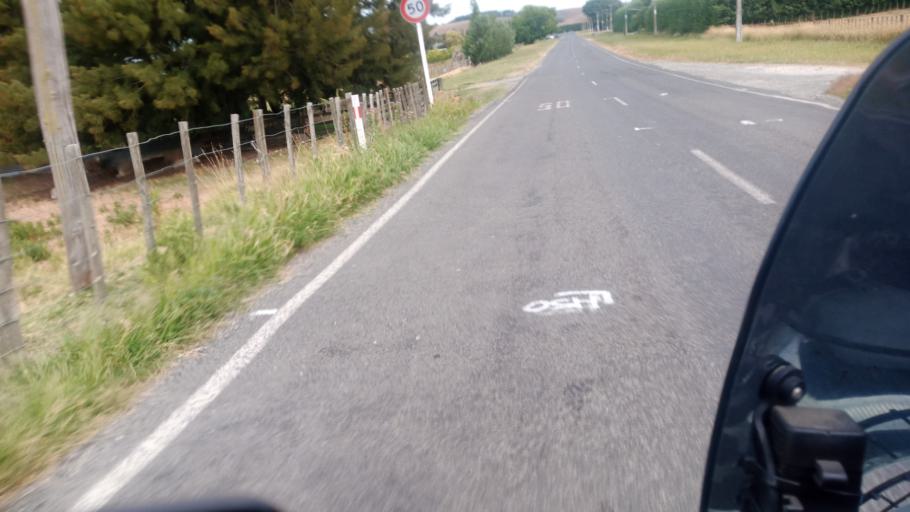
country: NZ
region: Gisborne
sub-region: Gisborne District
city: Gisborne
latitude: -38.6203
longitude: 177.8912
